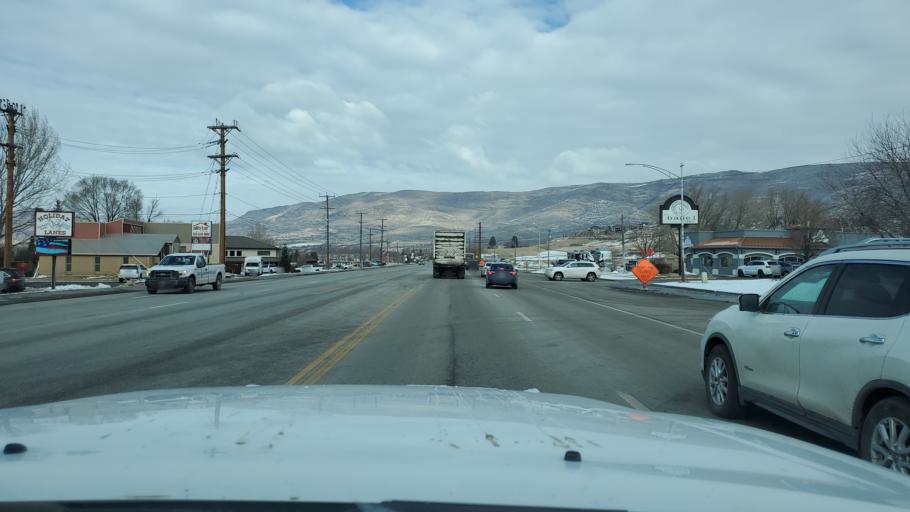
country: US
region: Utah
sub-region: Wasatch County
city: Heber
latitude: 40.5155
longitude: -111.4121
